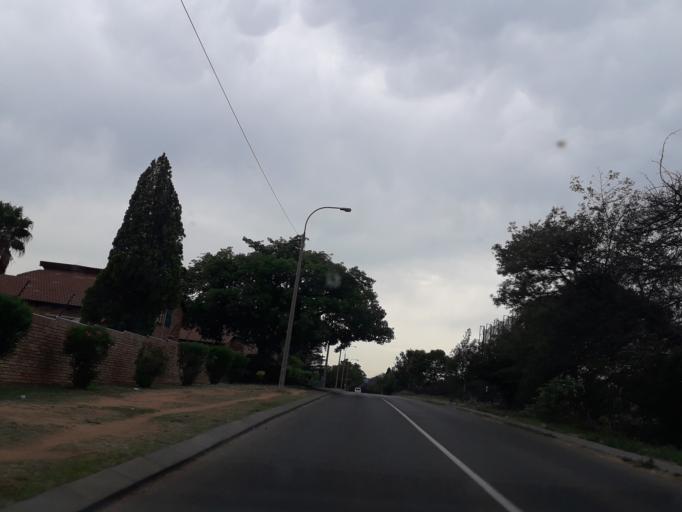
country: ZA
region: Gauteng
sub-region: City of Johannesburg Metropolitan Municipality
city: Roodepoort
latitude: -26.1083
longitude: 27.9186
